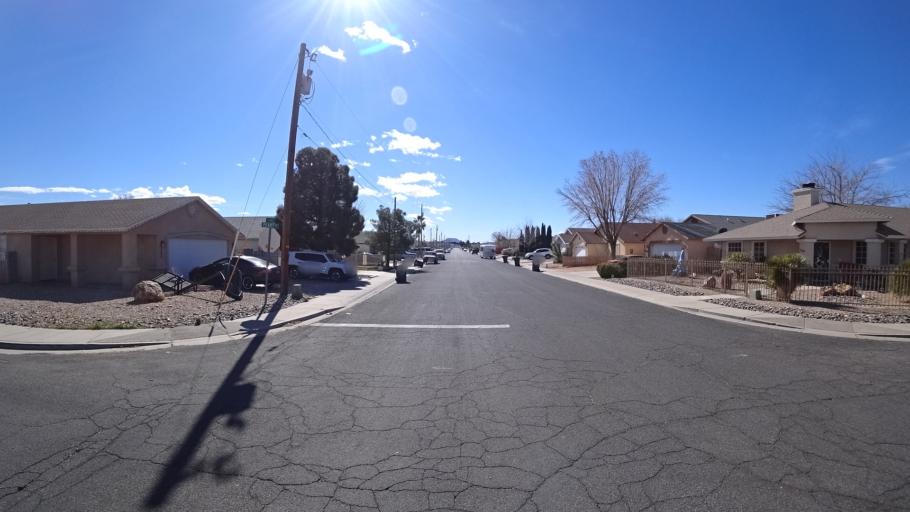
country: US
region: Arizona
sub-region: Mohave County
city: New Kingman-Butler
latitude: 35.2302
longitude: -114.0267
